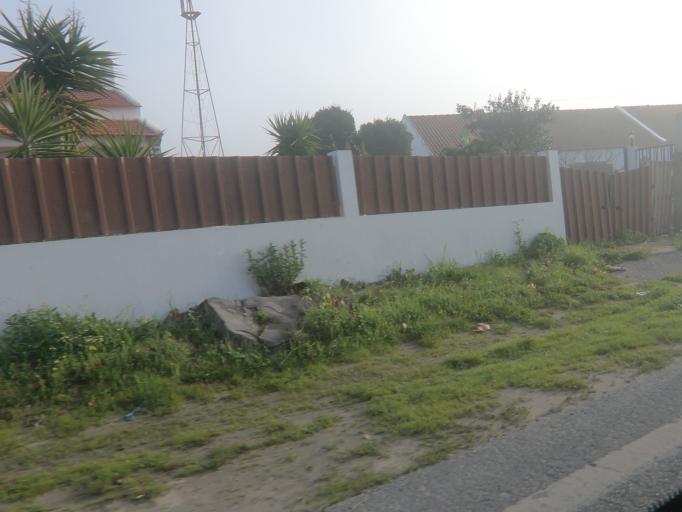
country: PT
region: Setubal
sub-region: Palmela
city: Pinhal Novo
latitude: 38.6743
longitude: -8.9339
